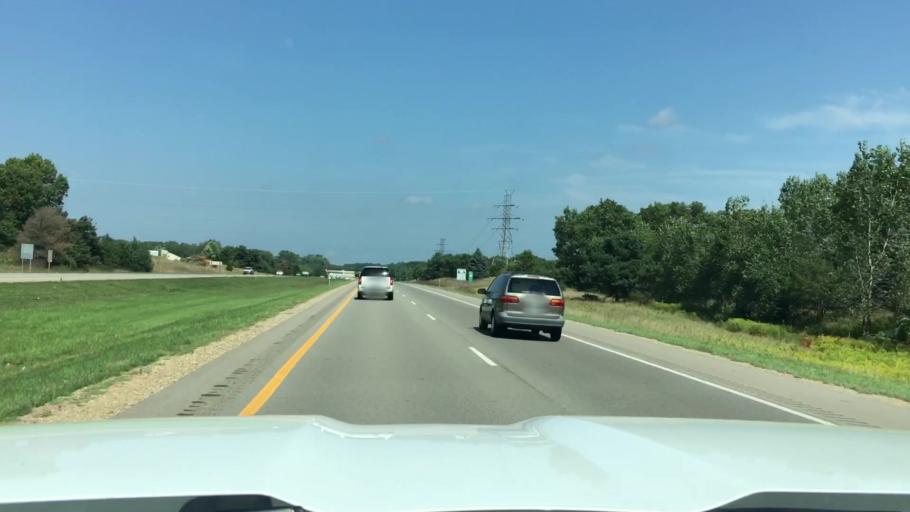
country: US
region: Michigan
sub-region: Kalamazoo County
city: Portage
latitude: 42.2218
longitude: -85.6405
